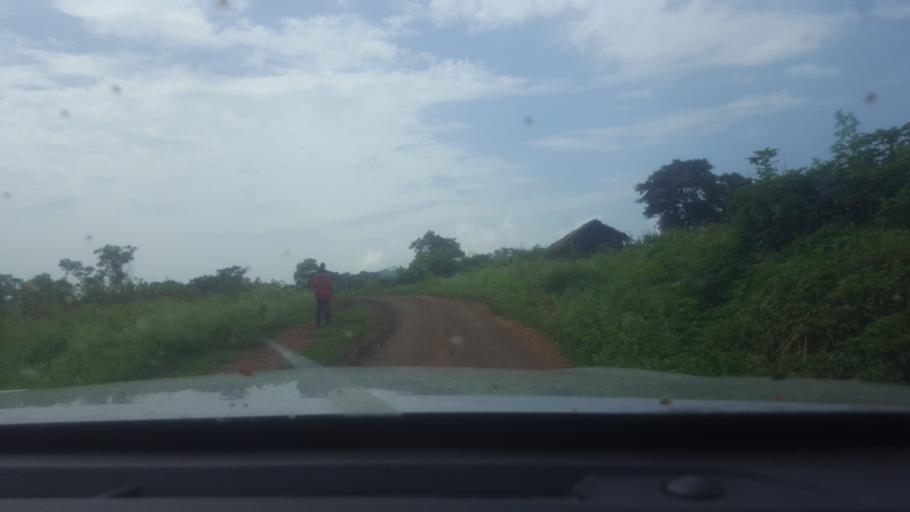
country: ET
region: Southern Nations, Nationalities, and People's Region
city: Tippi
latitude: 7.2776
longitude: 35.1511
